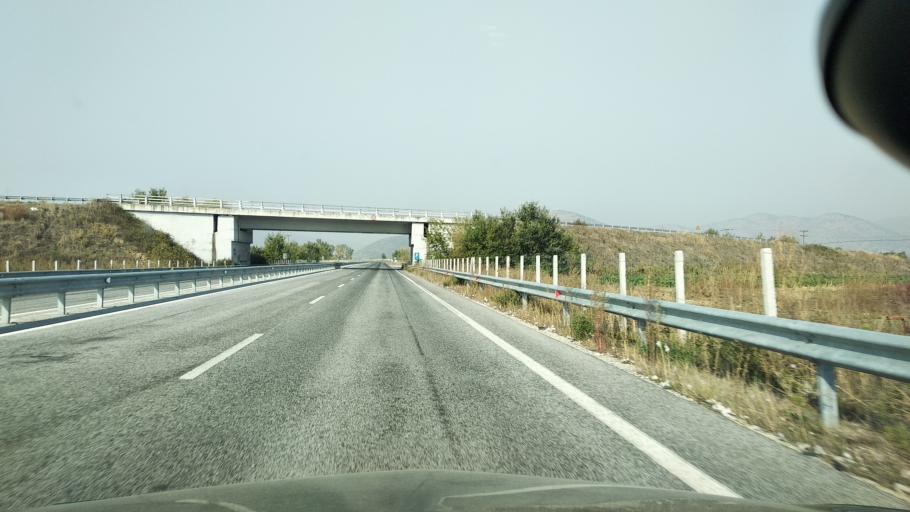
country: GR
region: Thessaly
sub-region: Trikala
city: Farkadona
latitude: 39.5837
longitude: 22.0495
